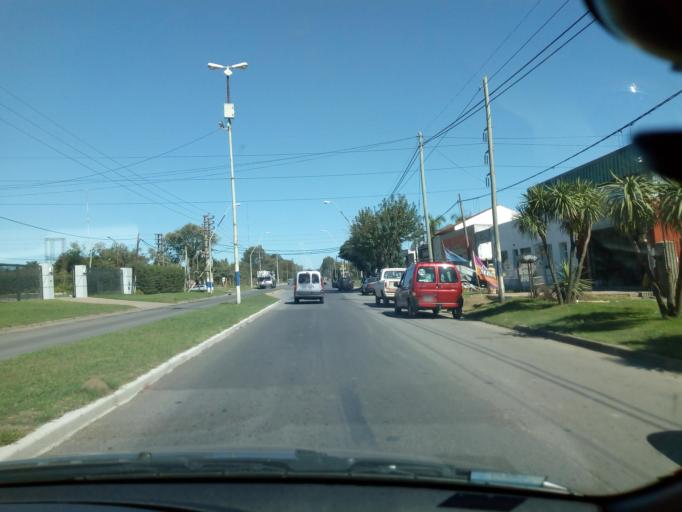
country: AR
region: Buenos Aires
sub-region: Partido de La Plata
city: La Plata
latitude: -34.9819
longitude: -57.9963
